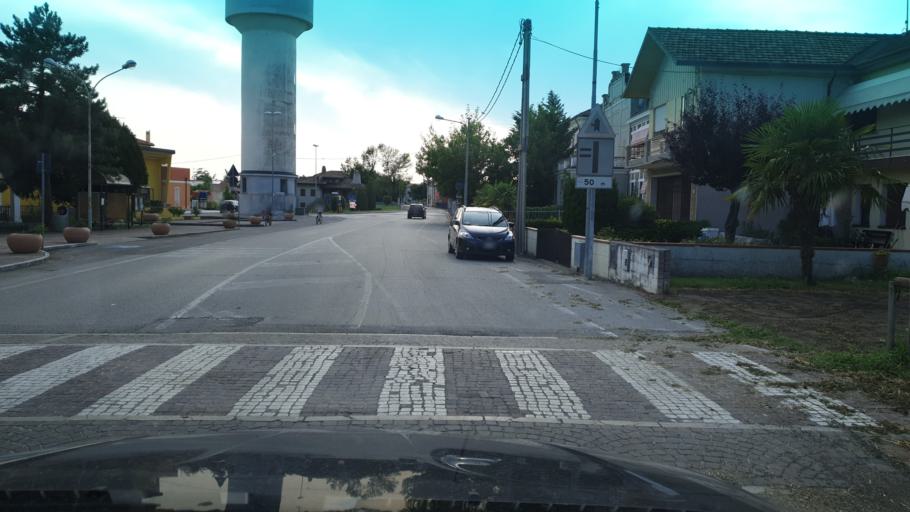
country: IT
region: Veneto
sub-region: Provincia di Rovigo
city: Castelguglielmo
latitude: 45.0257
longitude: 11.5374
